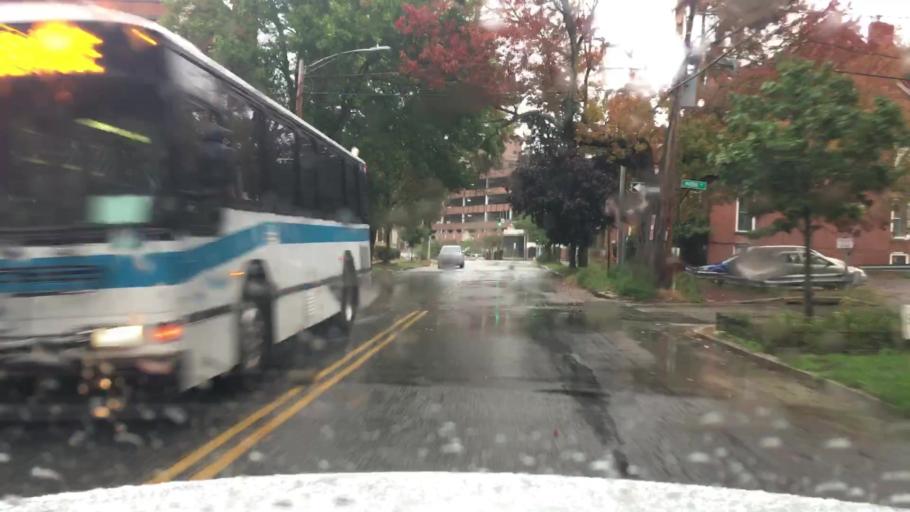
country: US
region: Maine
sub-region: Cumberland County
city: Portland
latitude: 43.6553
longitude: -70.2669
